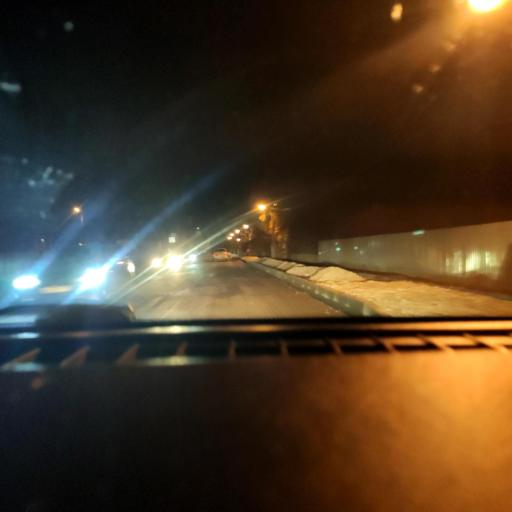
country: RU
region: Perm
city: Kondratovo
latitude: 57.9597
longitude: 56.1273
